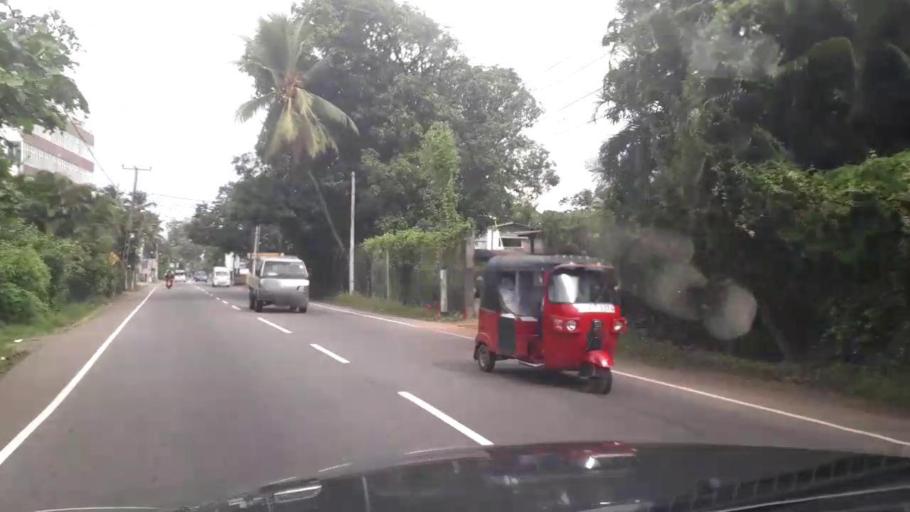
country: LK
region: Western
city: Panadura
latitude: 6.6807
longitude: 79.9218
